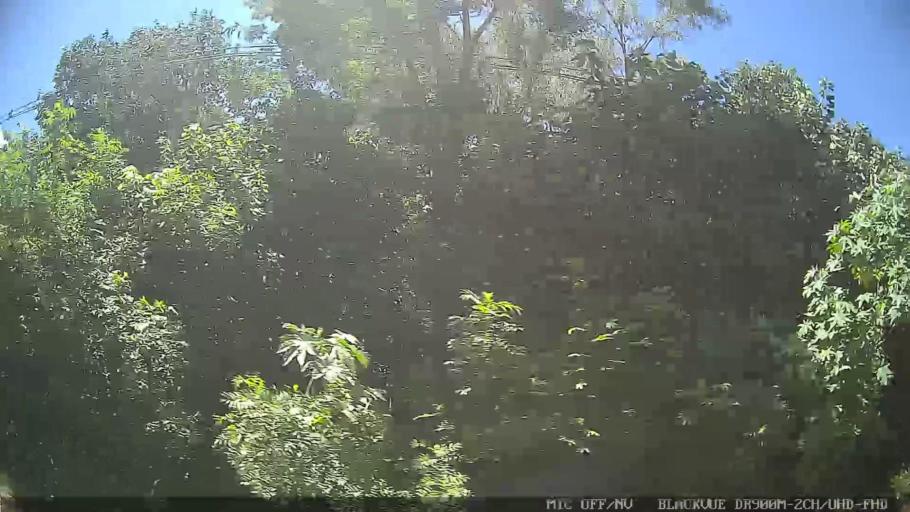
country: BR
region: Sao Paulo
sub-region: Biritiba-Mirim
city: Biritiba Mirim
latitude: -23.5667
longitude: -46.0936
